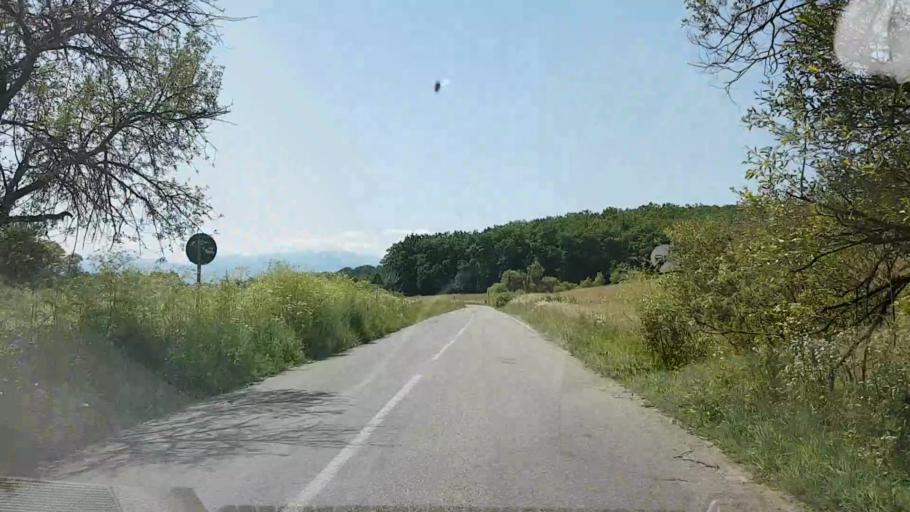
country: RO
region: Brasov
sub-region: Comuna Cincu
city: Cincu
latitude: 45.8841
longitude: 24.8141
